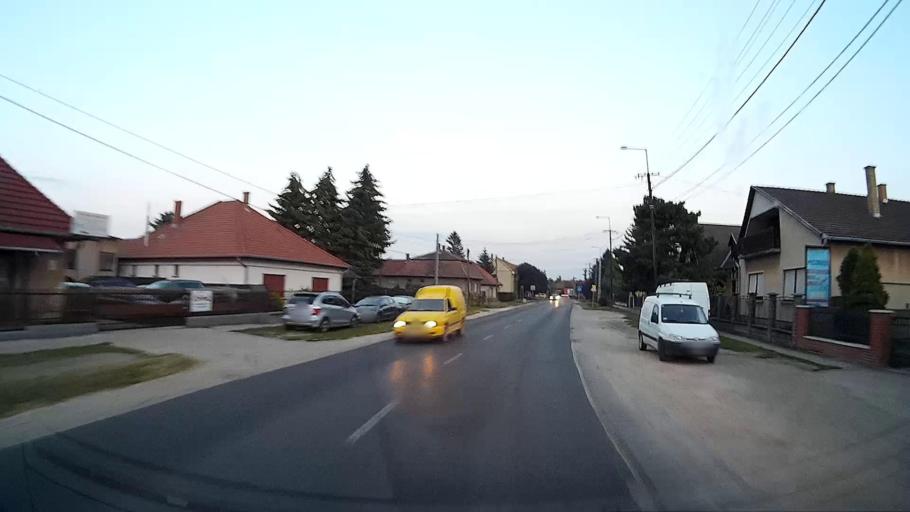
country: HU
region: Pest
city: Albertirsa
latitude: 47.2447
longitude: 19.6188
